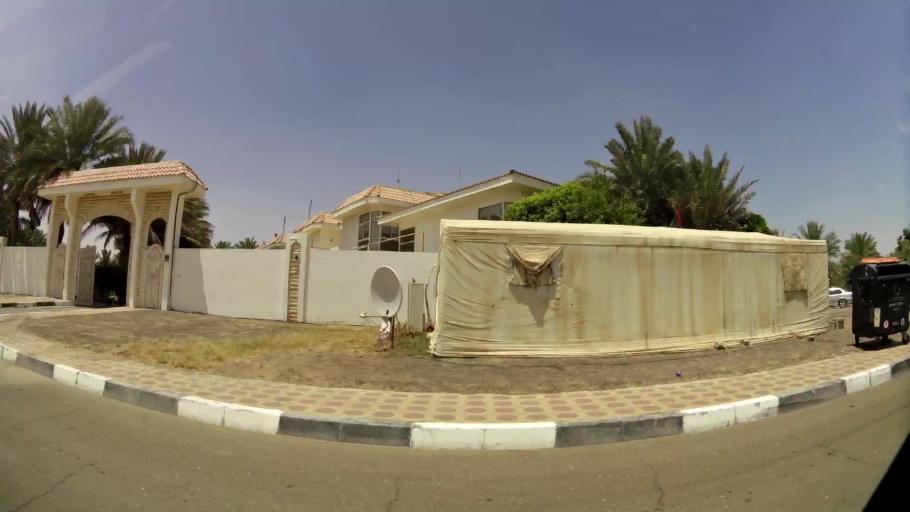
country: AE
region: Abu Dhabi
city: Al Ain
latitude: 24.2465
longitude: 55.6998
